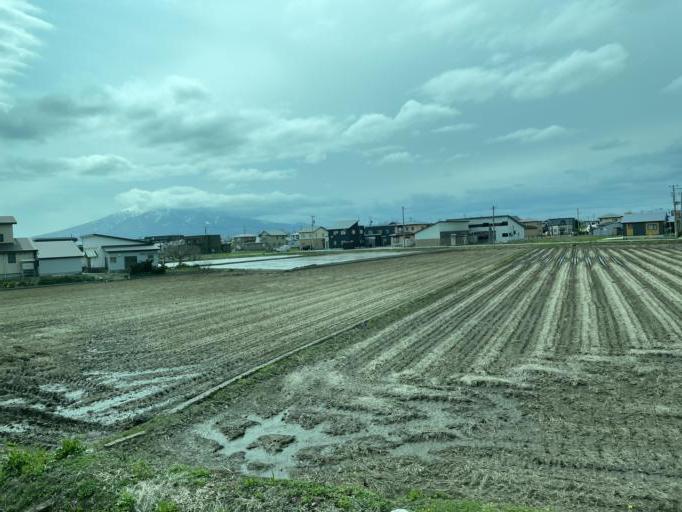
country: JP
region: Aomori
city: Goshogawara
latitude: 40.7668
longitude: 140.4348
